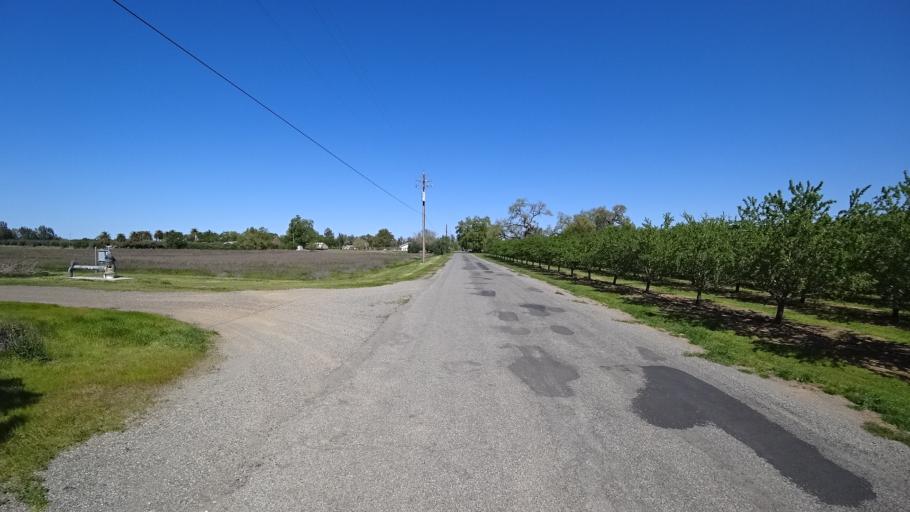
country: US
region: California
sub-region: Glenn County
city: Hamilton City
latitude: 39.7951
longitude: -122.0571
